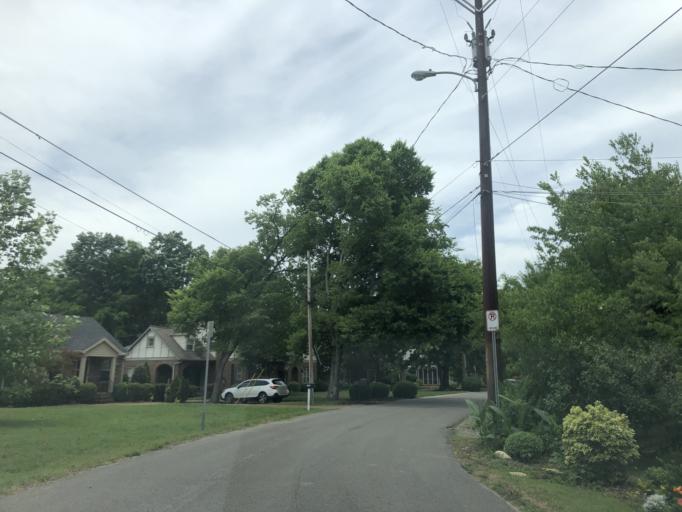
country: US
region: Tennessee
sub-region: Davidson County
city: Oak Hill
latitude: 36.1056
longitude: -86.8034
